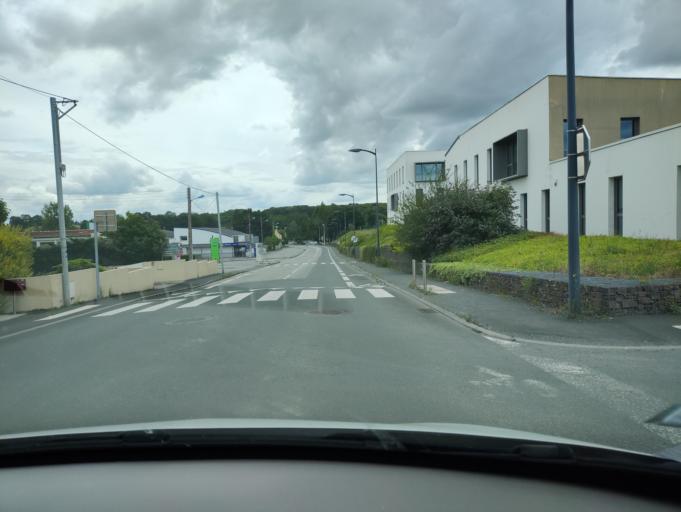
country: FR
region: Pays de la Loire
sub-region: Departement de la Loire-Atlantique
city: Chateaubriant
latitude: 47.7122
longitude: -1.3717
